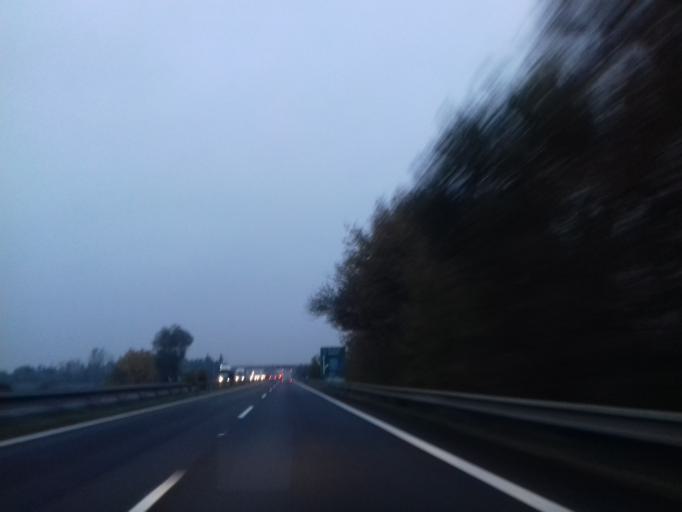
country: CZ
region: Olomoucky
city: Naklo
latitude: 49.6591
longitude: 17.1093
